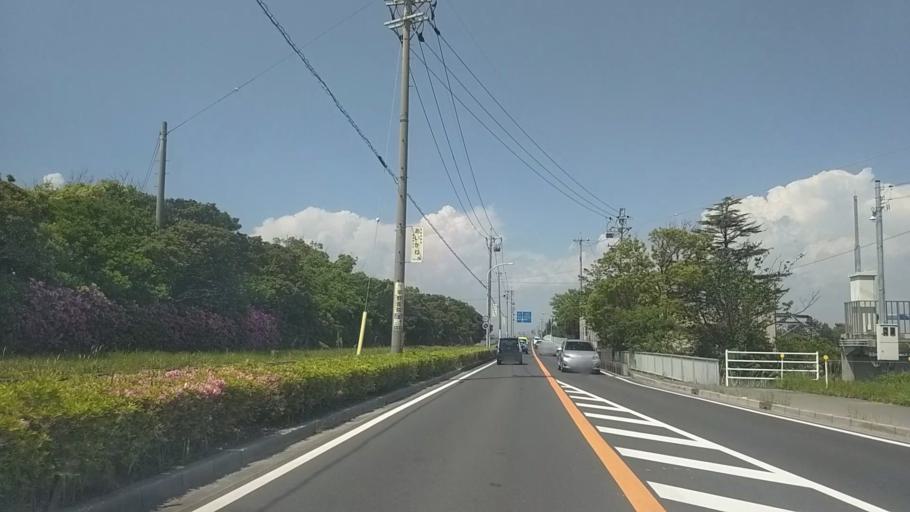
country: JP
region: Shizuoka
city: Kosai-shi
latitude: 34.6901
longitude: 137.6293
